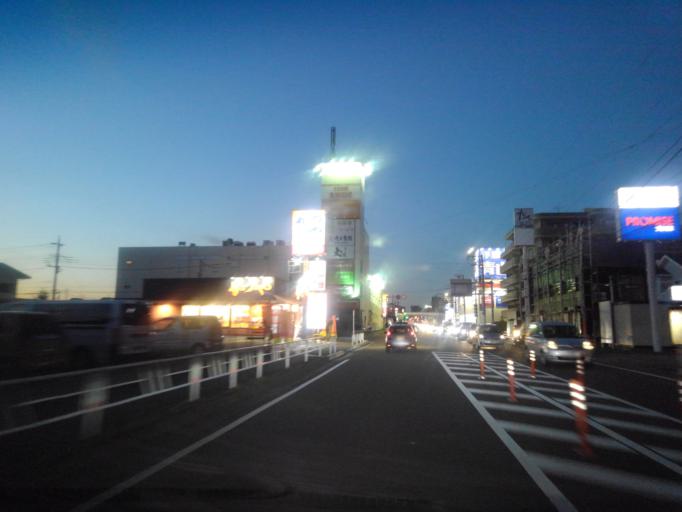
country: JP
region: Kanagawa
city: Minami-rinkan
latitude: 35.5067
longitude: 139.4627
